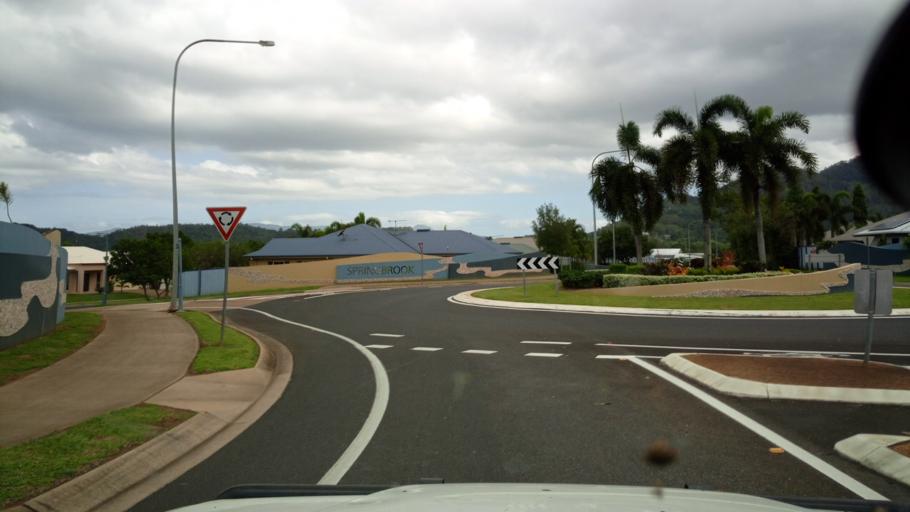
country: AU
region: Queensland
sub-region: Cairns
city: Redlynch
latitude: -16.8977
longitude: 145.6959
